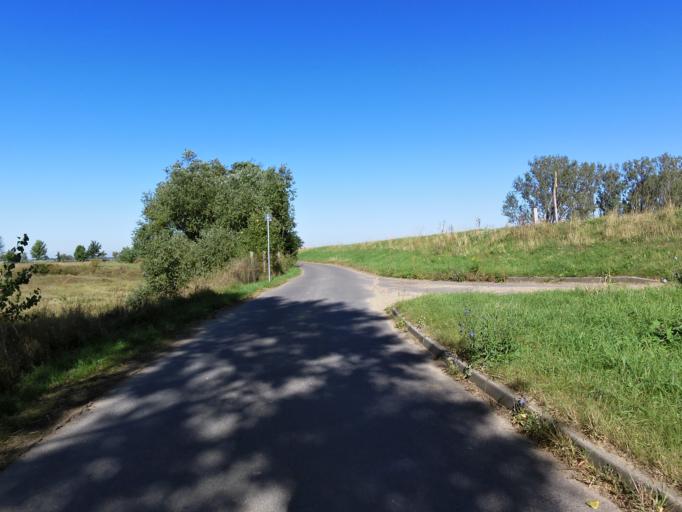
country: DE
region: Saxony
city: Elsnig
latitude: 51.6179
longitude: 12.9756
